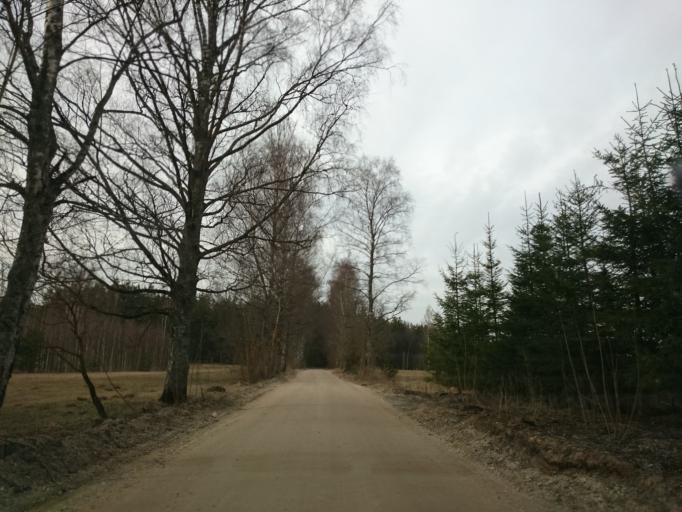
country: LV
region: Garkalne
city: Garkalne
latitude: 57.0168
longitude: 24.3870
